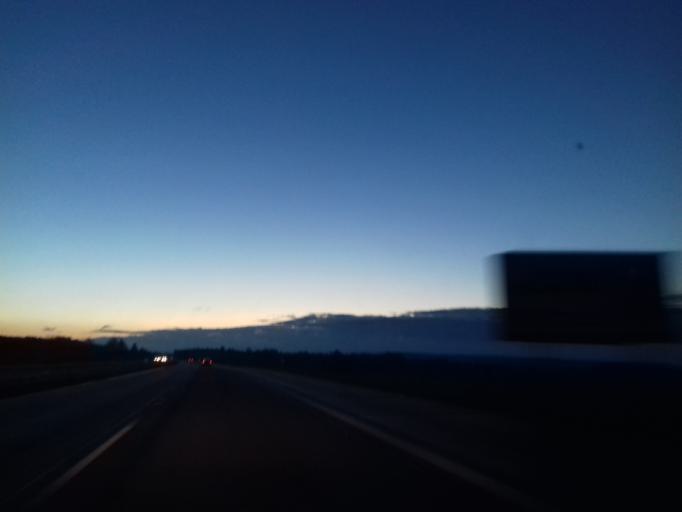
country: CZ
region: Vysocina
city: Krizanov
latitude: 49.3056
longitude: 16.1275
